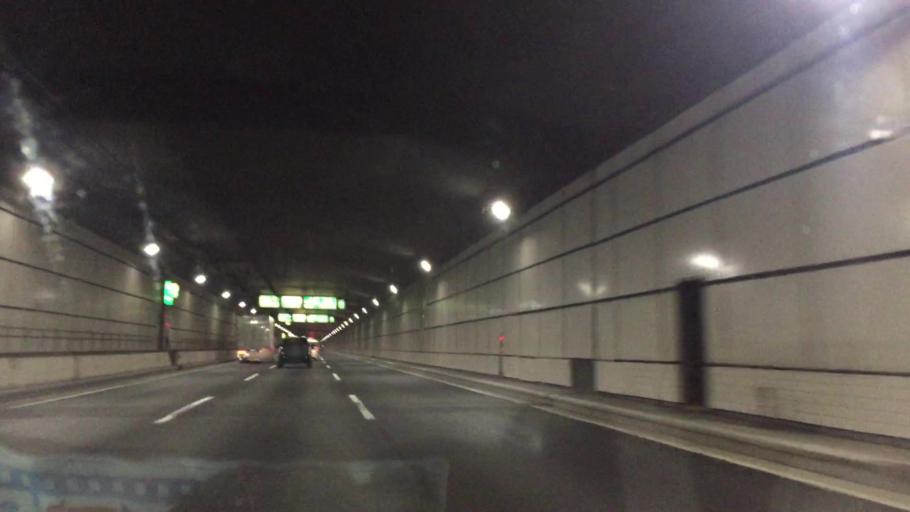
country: JP
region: Kanagawa
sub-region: Kawasaki-shi
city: Kawasaki
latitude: 35.5073
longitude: 139.7766
